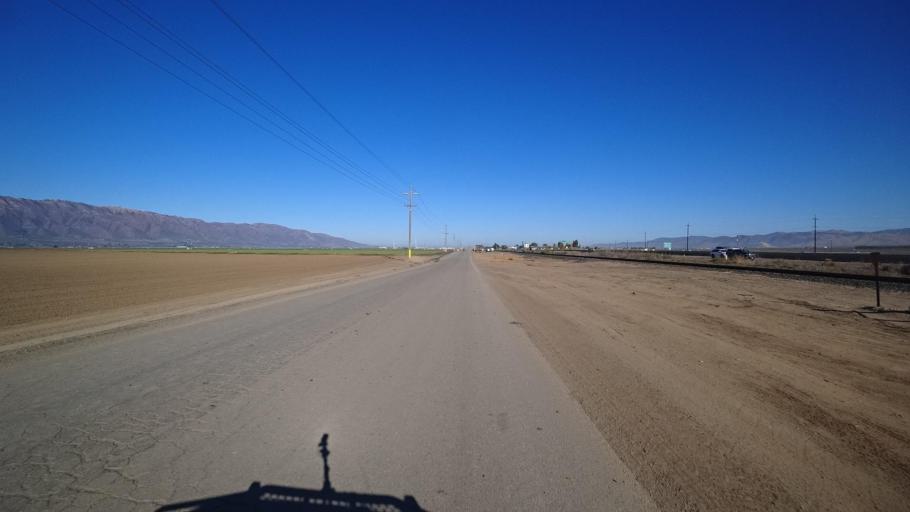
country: US
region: California
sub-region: Monterey County
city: Gonzales
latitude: 36.4882
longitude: -121.4206
